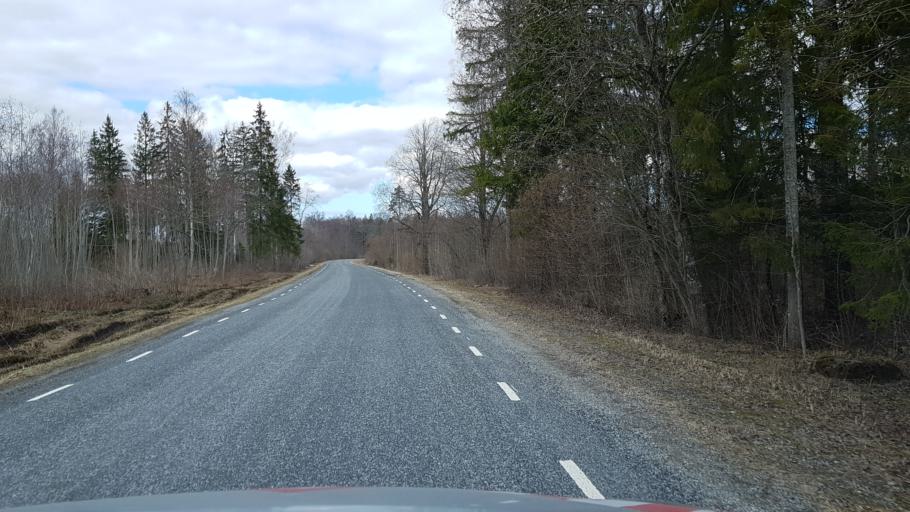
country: EE
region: Laeaene-Virumaa
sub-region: Tamsalu vald
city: Tamsalu
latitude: 59.1879
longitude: 26.1302
